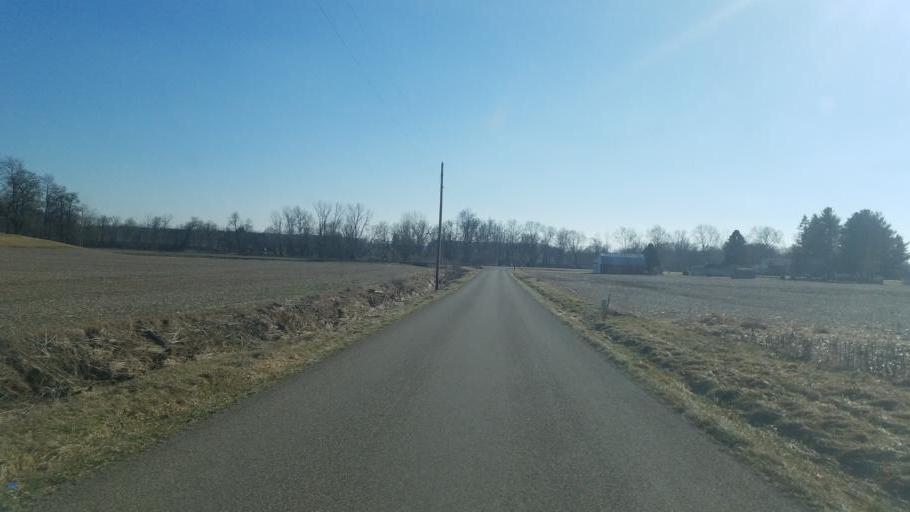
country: US
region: Ohio
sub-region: Knox County
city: Fredericktown
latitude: 40.4652
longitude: -82.6265
